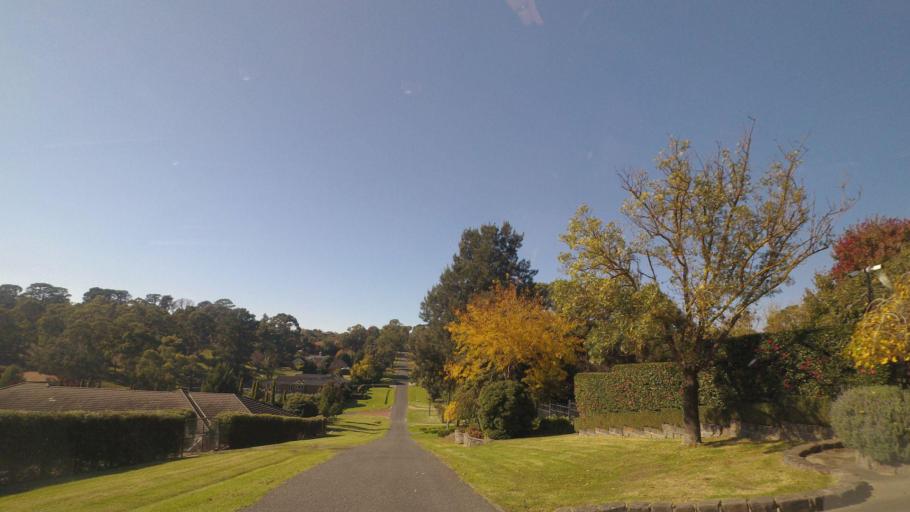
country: AU
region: Victoria
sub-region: Nillumbik
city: Eltham
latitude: -37.7472
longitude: 145.1526
